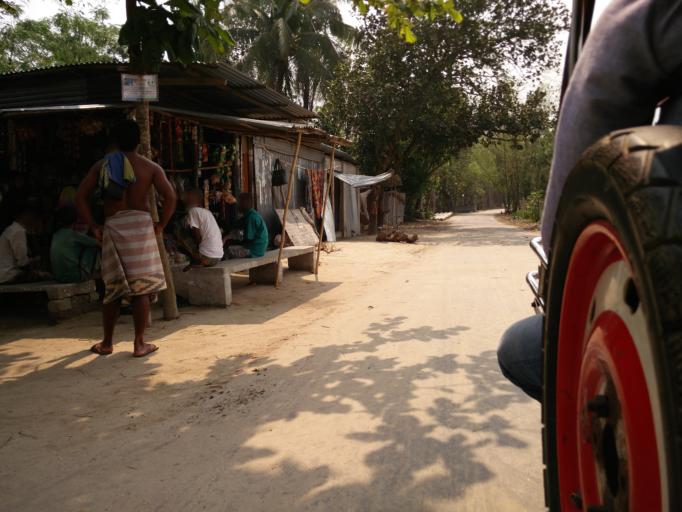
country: BD
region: Dhaka
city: Muktagacha
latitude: 24.8933
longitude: 90.2642
